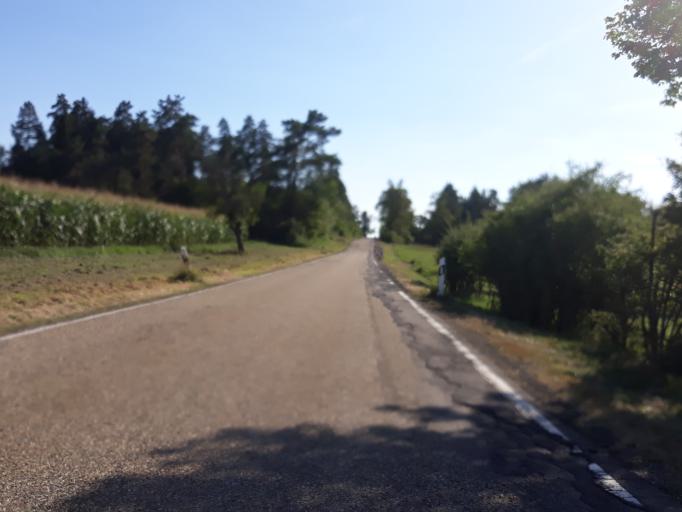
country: DE
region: Baden-Wuerttemberg
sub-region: Regierungsbezirk Stuttgart
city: Deckenpfronn
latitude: 48.6683
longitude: 8.8447
